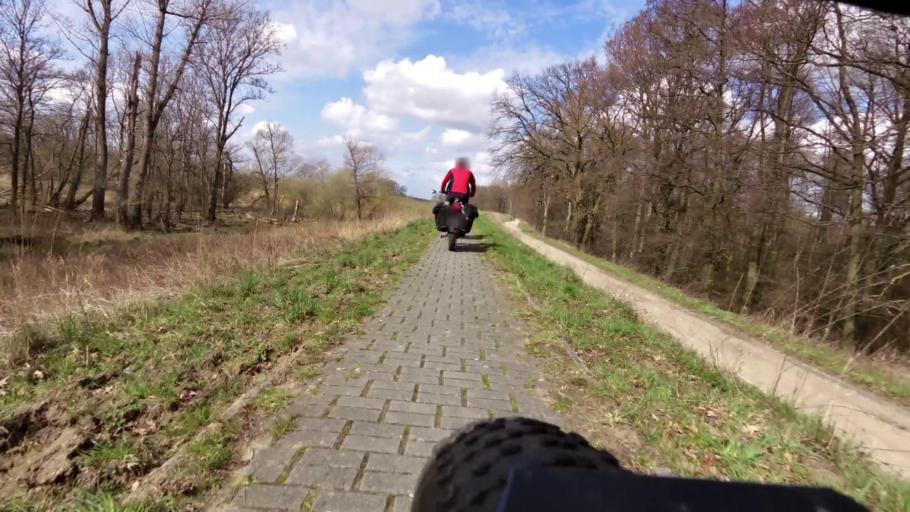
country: PL
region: Lubusz
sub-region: Powiat slubicki
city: Slubice
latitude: 52.3756
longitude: 14.5574
